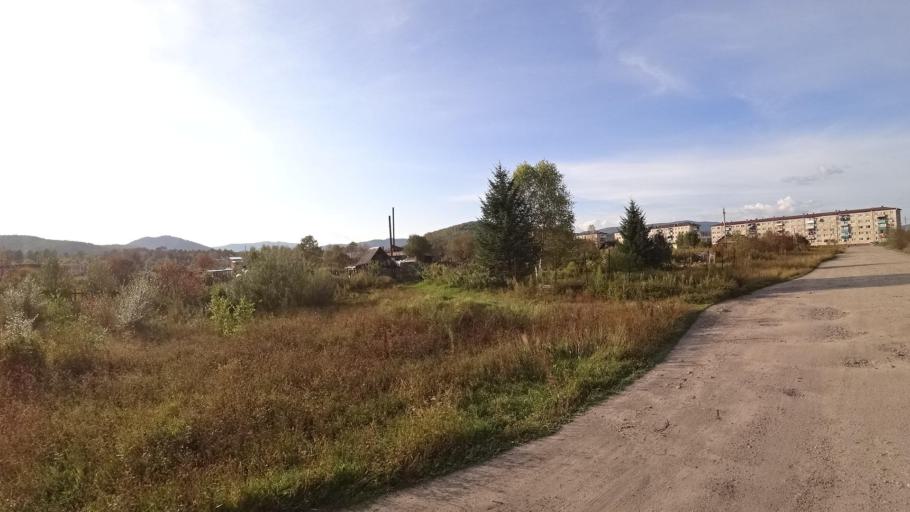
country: RU
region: Jewish Autonomous Oblast
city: Kul'dur
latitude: 49.1993
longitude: 131.6258
